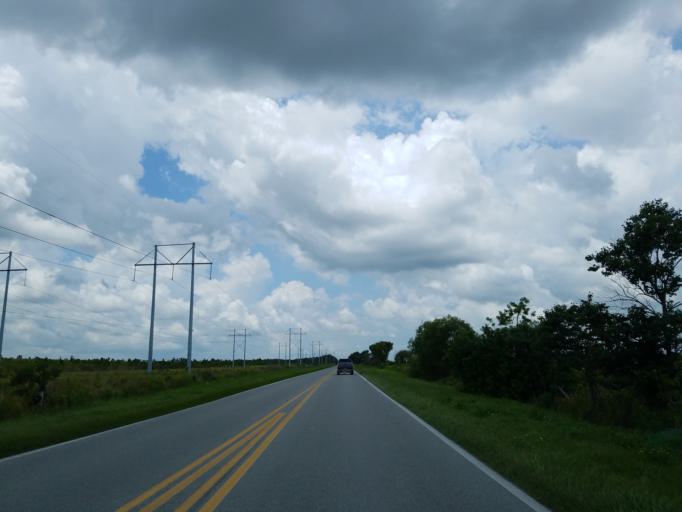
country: US
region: Florida
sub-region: Polk County
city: Fuller Heights
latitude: 27.8508
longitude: -82.0284
